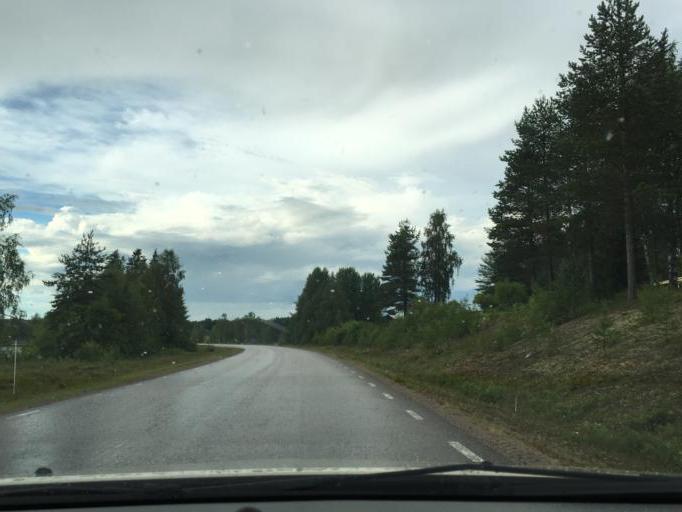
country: SE
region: Norrbotten
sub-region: Kalix Kommun
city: Toere
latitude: 66.0006
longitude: 22.8548
